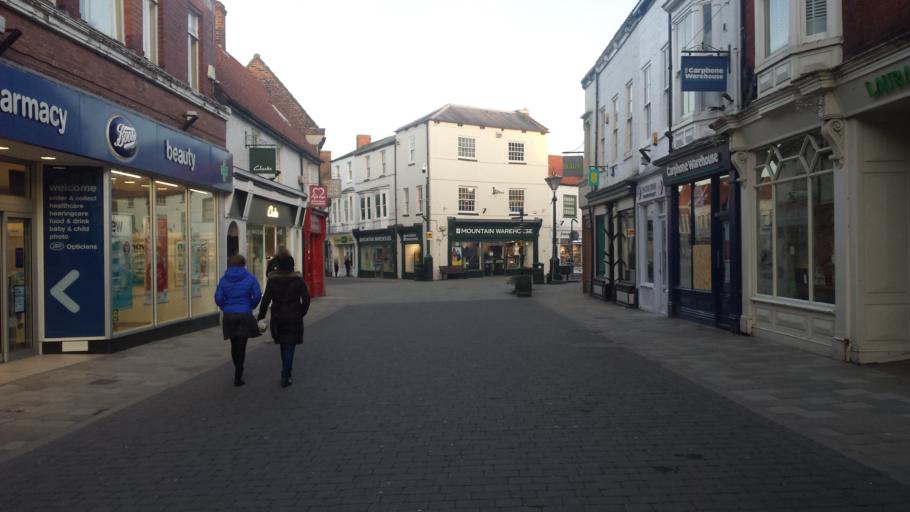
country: GB
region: England
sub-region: East Riding of Yorkshire
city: Beverley
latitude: 53.8418
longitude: -0.4299
